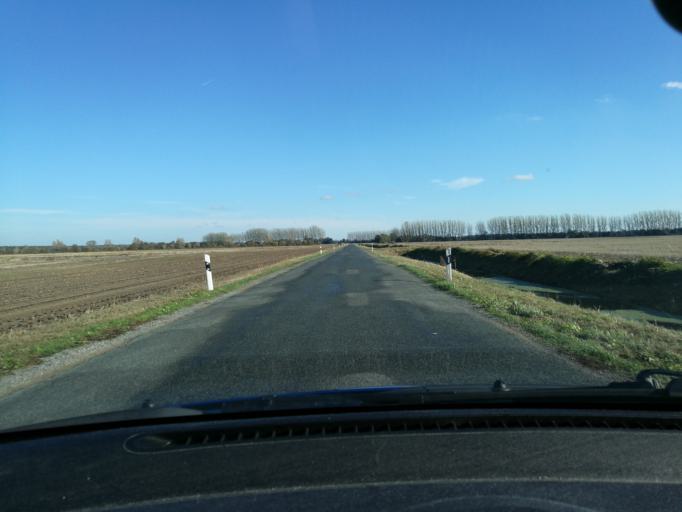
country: DE
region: Mecklenburg-Vorpommern
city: Neu Kaliss
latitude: 53.1471
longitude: 11.2917
